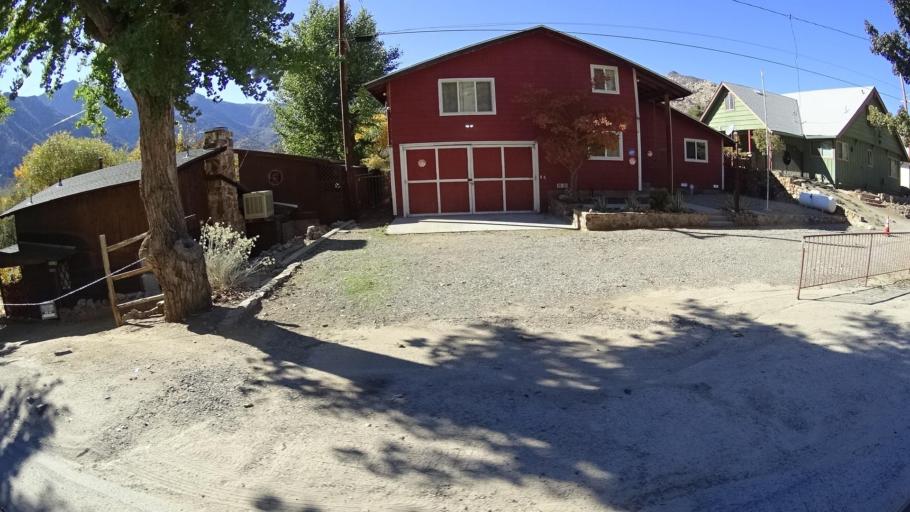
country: US
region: California
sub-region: Kern County
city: Kernville
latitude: 35.7858
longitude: -118.4464
